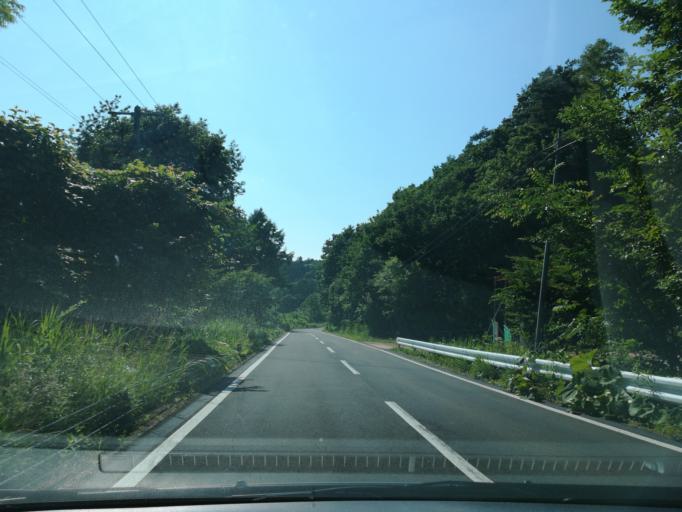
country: JP
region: Hokkaido
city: Chitose
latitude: 42.9104
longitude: 141.7324
